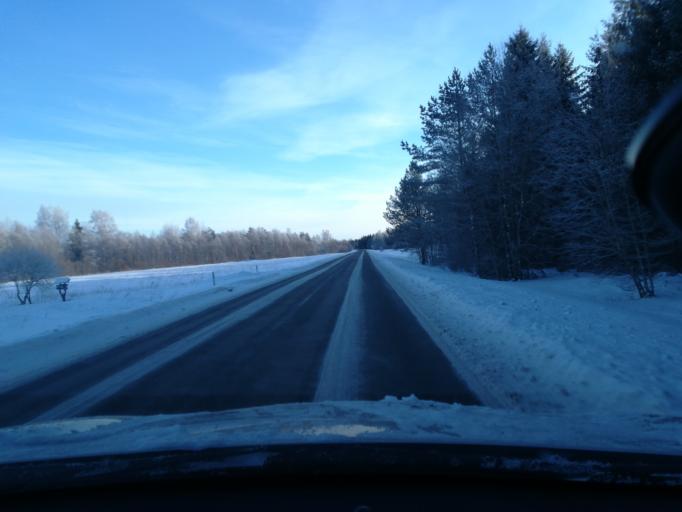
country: EE
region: Harju
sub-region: Keila linn
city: Keila
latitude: 59.3797
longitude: 24.4527
